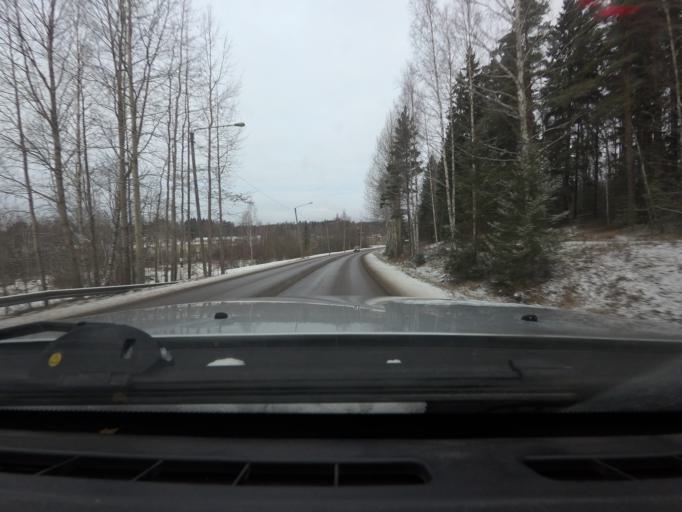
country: FI
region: Uusimaa
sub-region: Helsinki
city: Kilo
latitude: 60.2347
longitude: 24.7720
